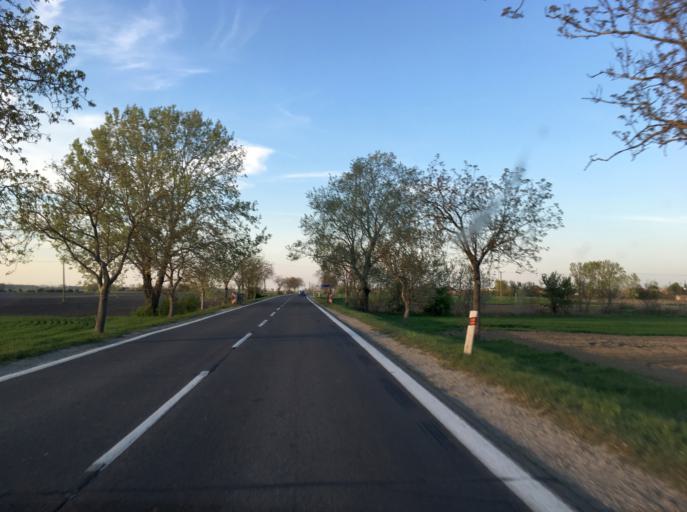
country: SK
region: Trnavsky
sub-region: Okres Dunajska Streda
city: Velky Meder
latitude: 47.8462
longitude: 17.7321
